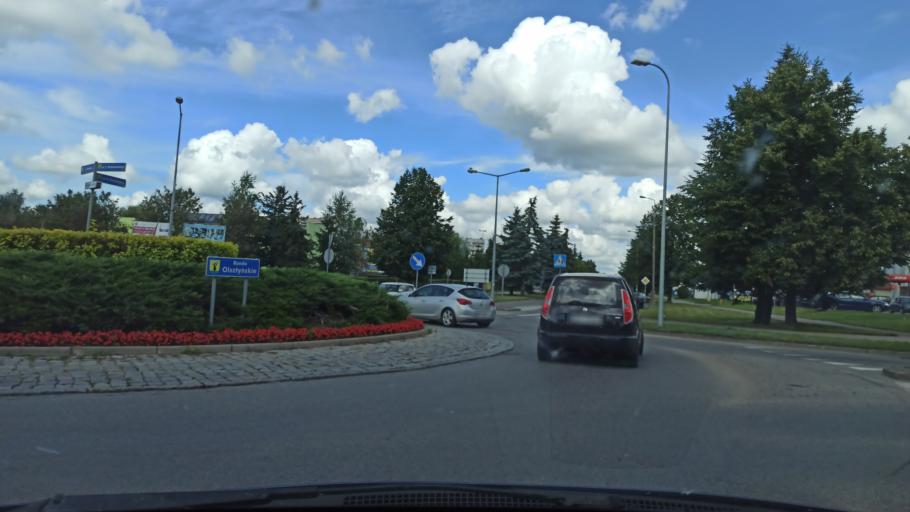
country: PL
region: Warmian-Masurian Voivodeship
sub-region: Powiat ostrodzki
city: Morag
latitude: 53.9074
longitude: 19.9365
